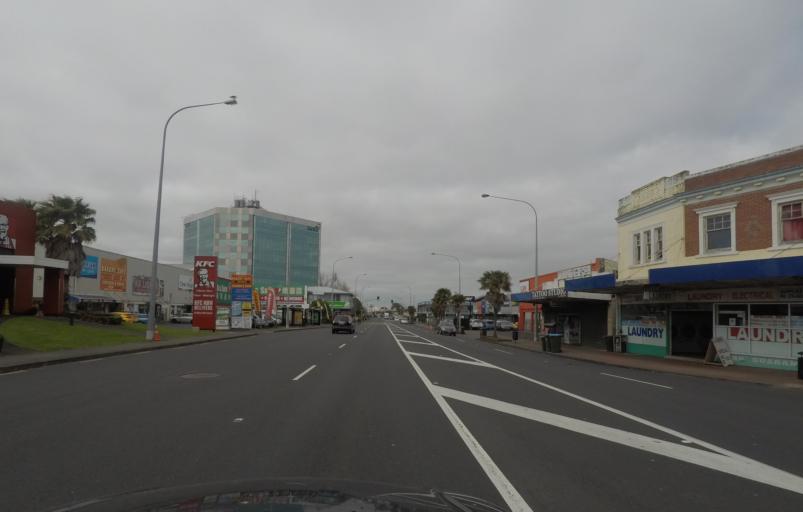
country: NZ
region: Auckland
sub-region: Auckland
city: Mangere
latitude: -36.9457
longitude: 174.8452
